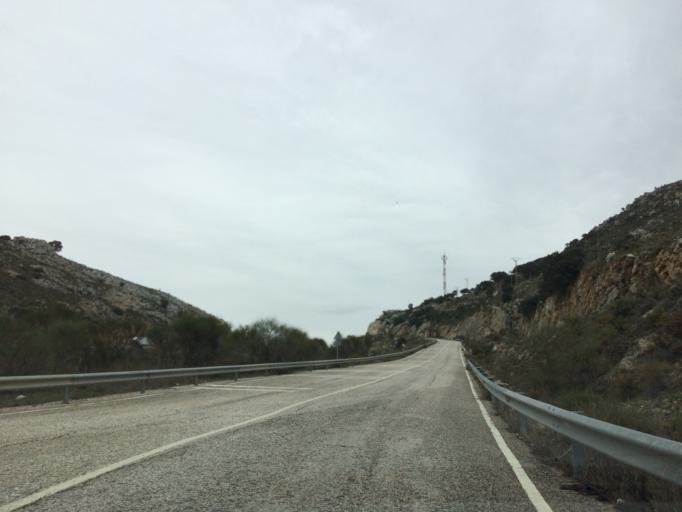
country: ES
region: Andalusia
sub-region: Provincia de Malaga
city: Casabermeja
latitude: 36.9622
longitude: -4.4448
